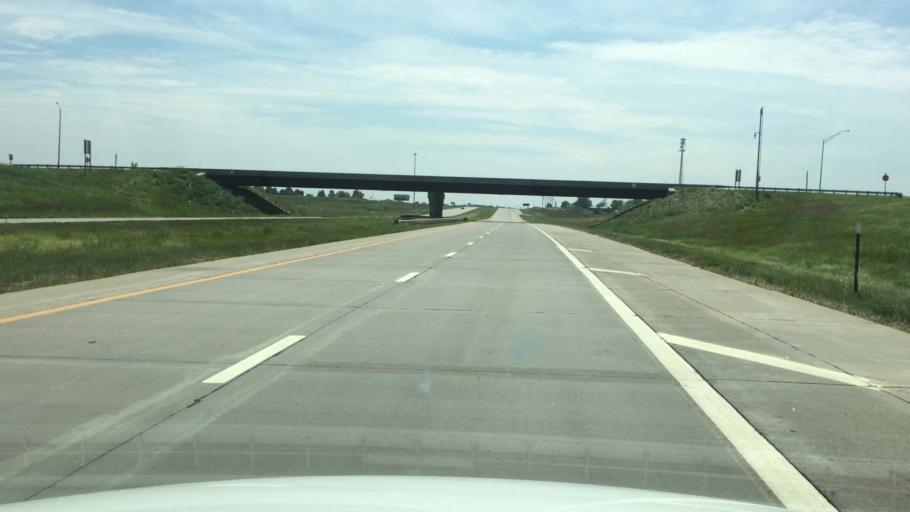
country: US
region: Kansas
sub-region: Jackson County
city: Holton
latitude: 39.3204
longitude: -95.7200
